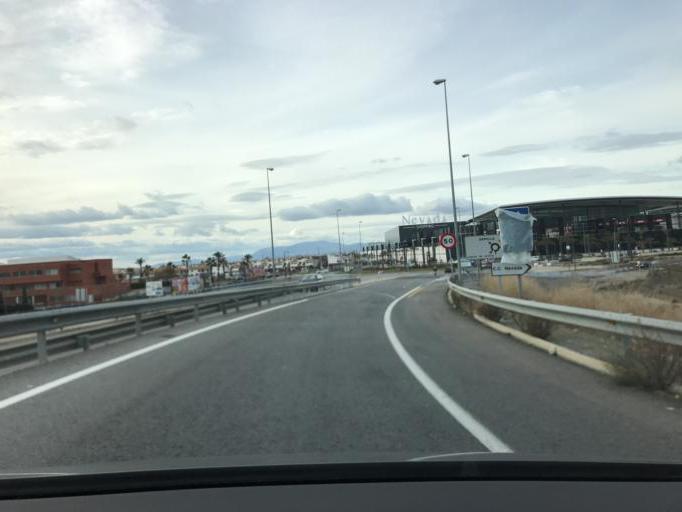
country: ES
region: Andalusia
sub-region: Provincia de Granada
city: Armilla
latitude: 37.1424
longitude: -3.6117
